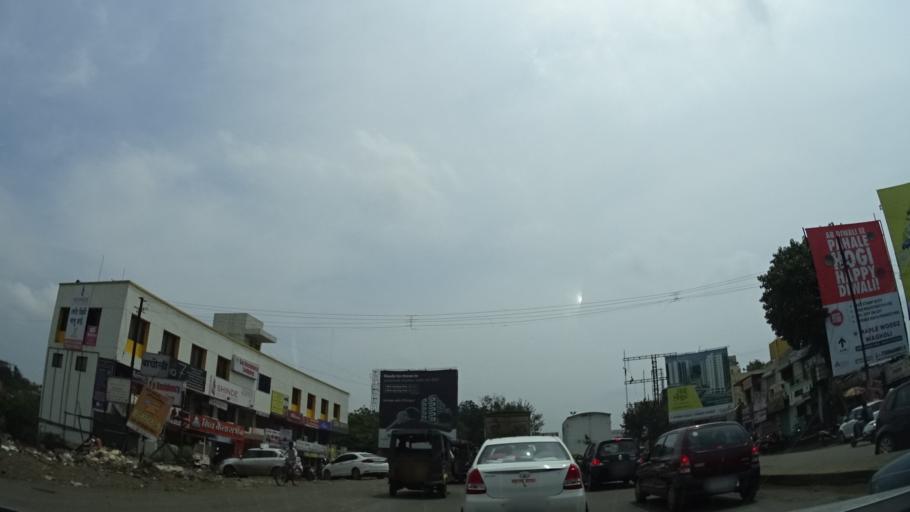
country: IN
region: Maharashtra
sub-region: Pune Division
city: Lohogaon
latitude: 18.5808
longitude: 73.9803
